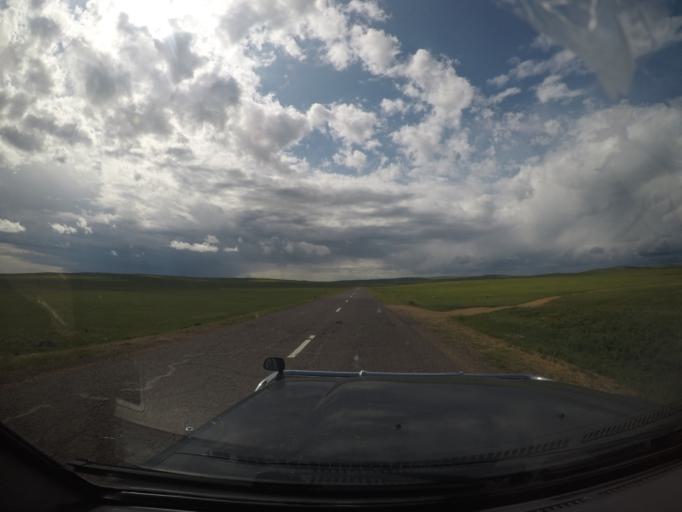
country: MN
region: Hentiy
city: Bayanbulag
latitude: 47.4620
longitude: 109.6250
